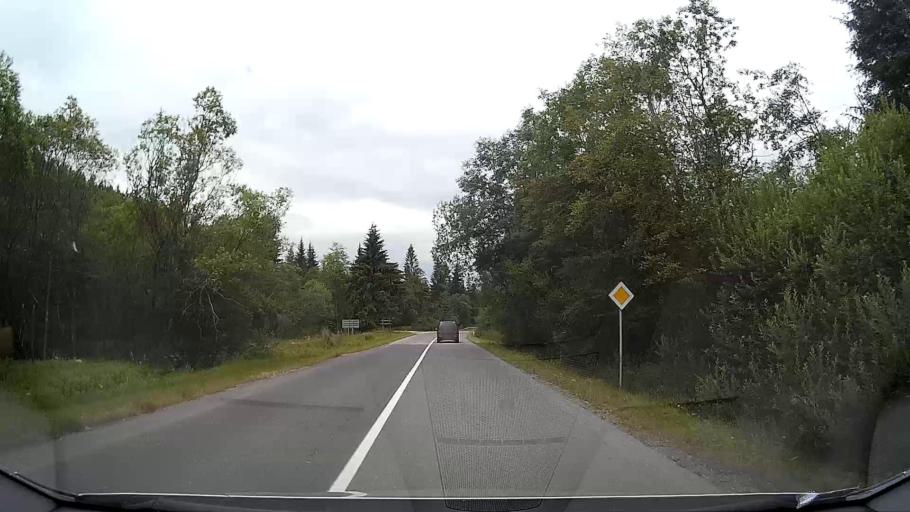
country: SK
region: Kosicky
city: Dobsina
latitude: 48.8848
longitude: 20.2390
